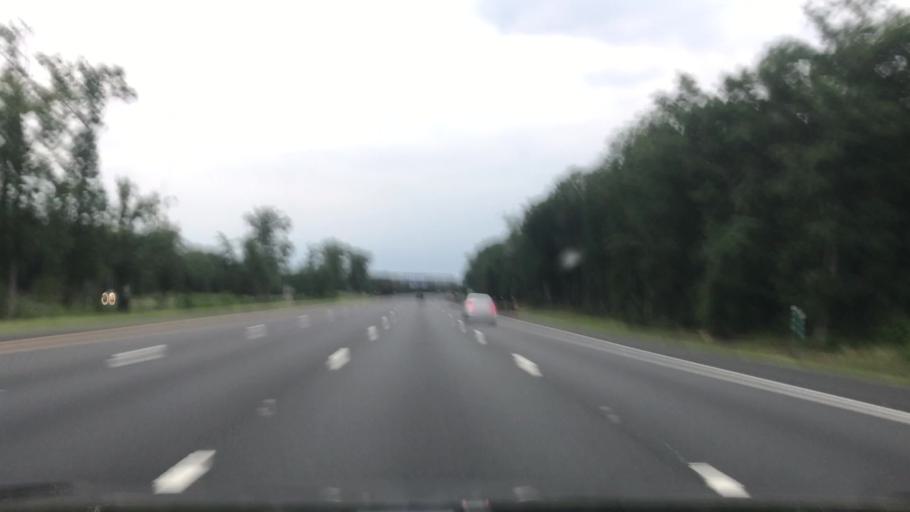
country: US
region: New Jersey
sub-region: Monmouth County
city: Ramtown
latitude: 40.1216
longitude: -74.1270
